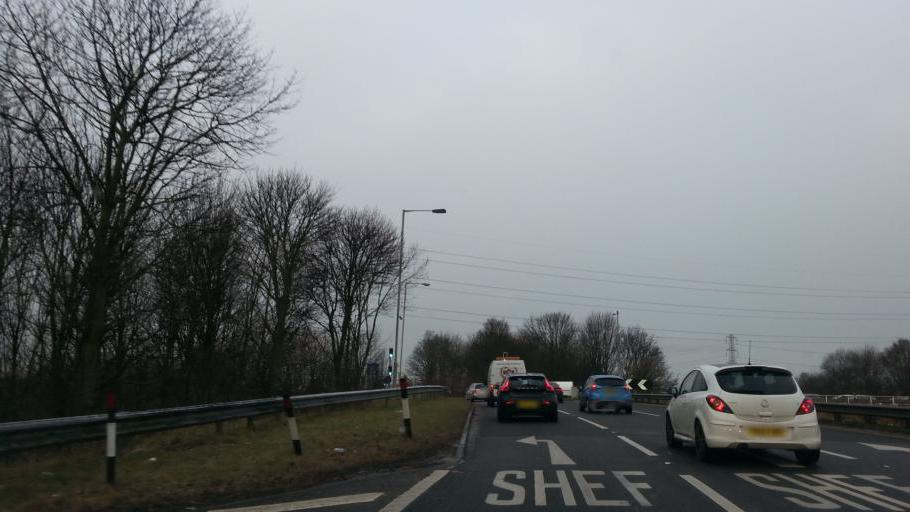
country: GB
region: England
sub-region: Rotherham
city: Treeton
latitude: 53.3984
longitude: -1.3472
